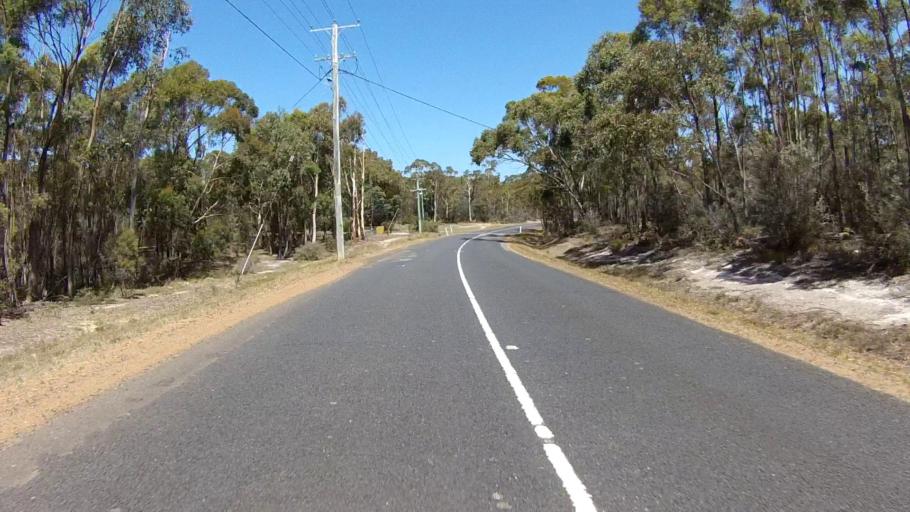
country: AU
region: Tasmania
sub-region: Clarence
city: Sandford
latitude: -42.9800
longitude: 147.4849
